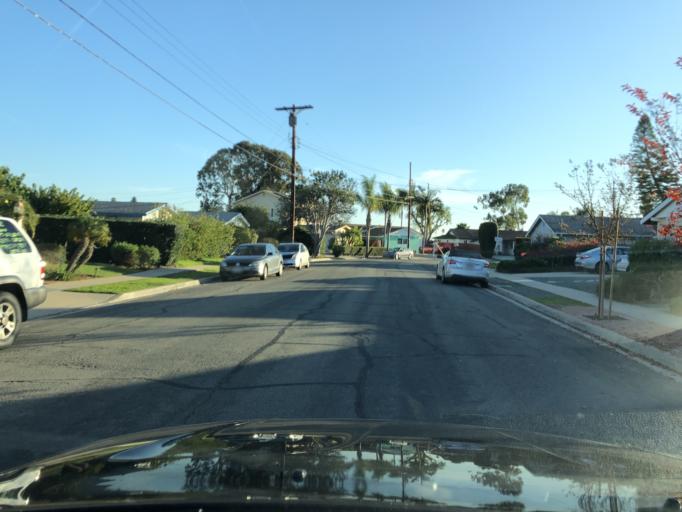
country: US
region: California
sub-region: San Diego County
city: La Jolla
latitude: 32.8194
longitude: -117.1931
